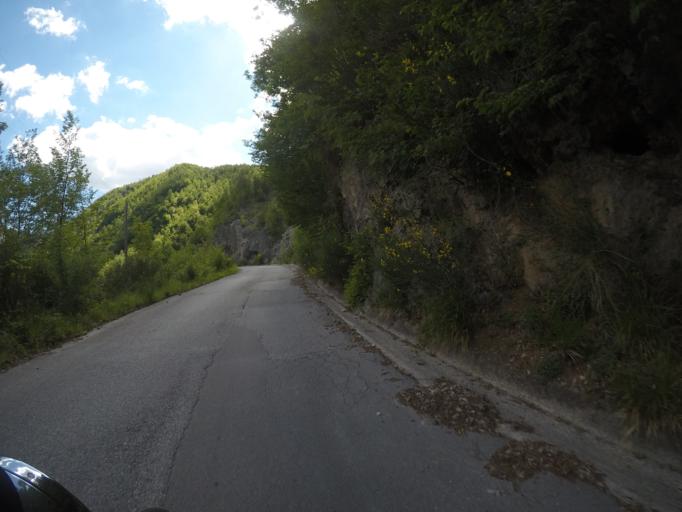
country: IT
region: Tuscany
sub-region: Provincia di Lucca
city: Minucciano
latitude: 44.1603
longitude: 10.2021
